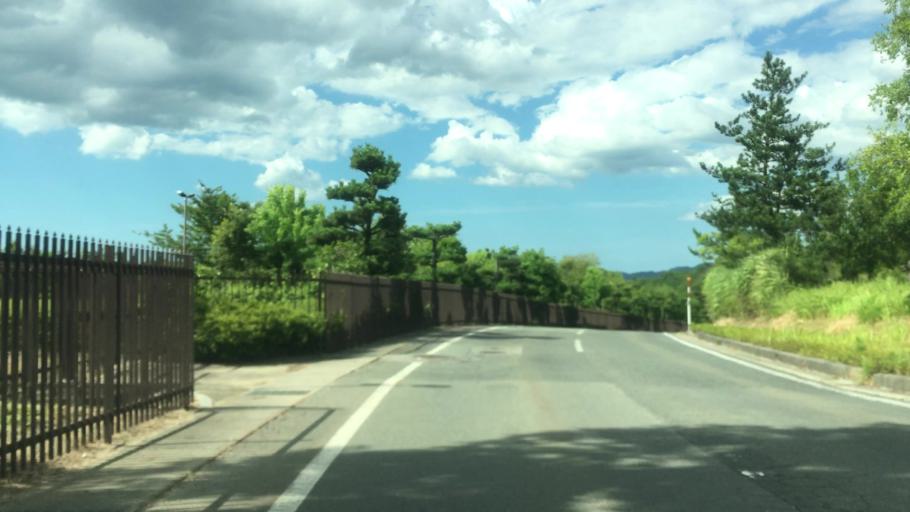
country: JP
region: Hyogo
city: Toyooka
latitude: 35.5179
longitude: 134.7902
